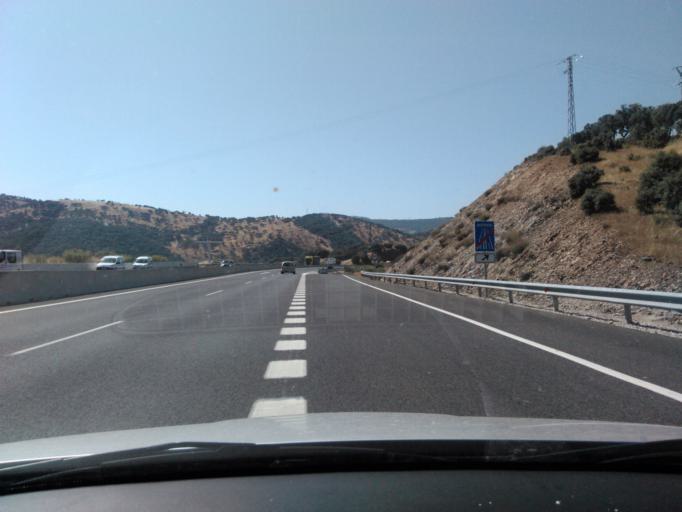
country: ES
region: Andalusia
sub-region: Provincia de Jaen
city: Santa Elena
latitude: 38.4168
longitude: -3.4998
